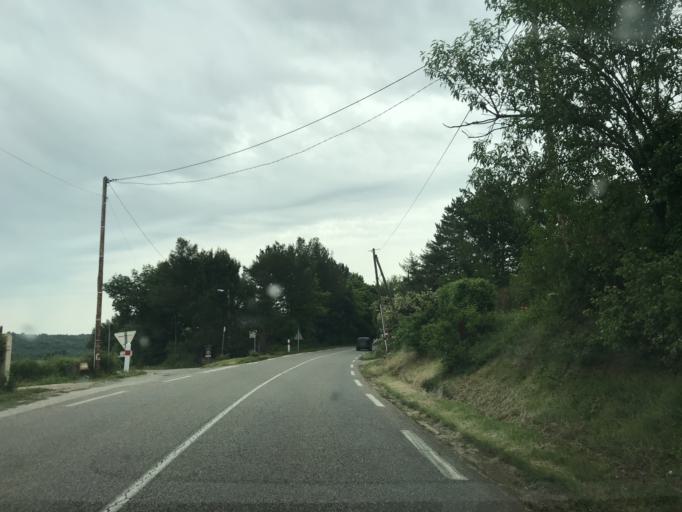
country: FR
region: Provence-Alpes-Cote d'Azur
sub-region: Departement du Var
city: Rians
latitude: 43.6268
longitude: 5.7680
